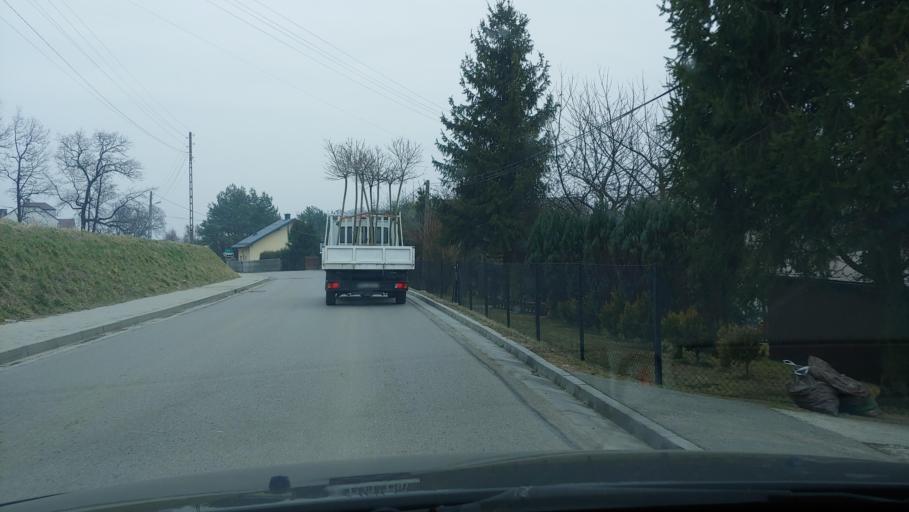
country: PL
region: Lesser Poland Voivodeship
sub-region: Powiat krakowski
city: Balice
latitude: 50.0917
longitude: 19.7784
